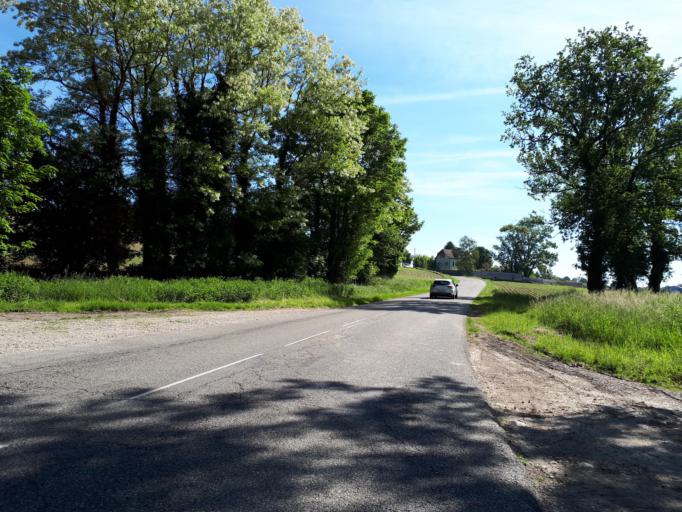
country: FR
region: Rhone-Alpes
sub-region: Departement de l'Isere
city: Saint-Savin
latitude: 45.6119
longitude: 5.3131
